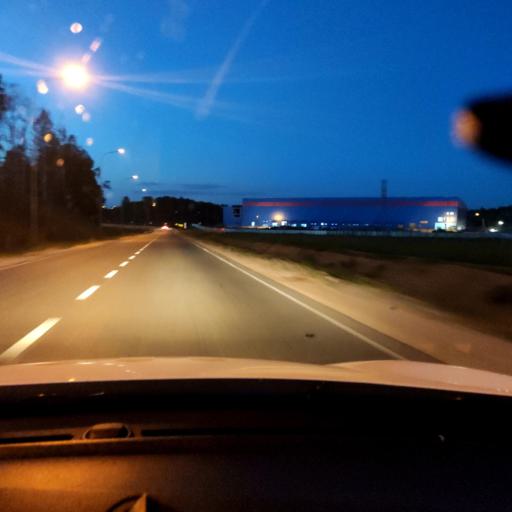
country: RU
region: Tatarstan
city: Osinovo
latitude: 55.8538
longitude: 48.8431
